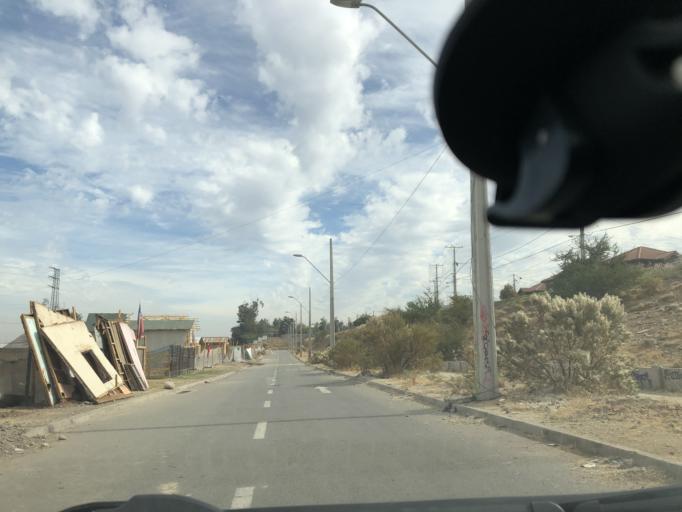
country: CL
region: Santiago Metropolitan
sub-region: Provincia de Cordillera
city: Puente Alto
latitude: -33.6142
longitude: -70.5282
